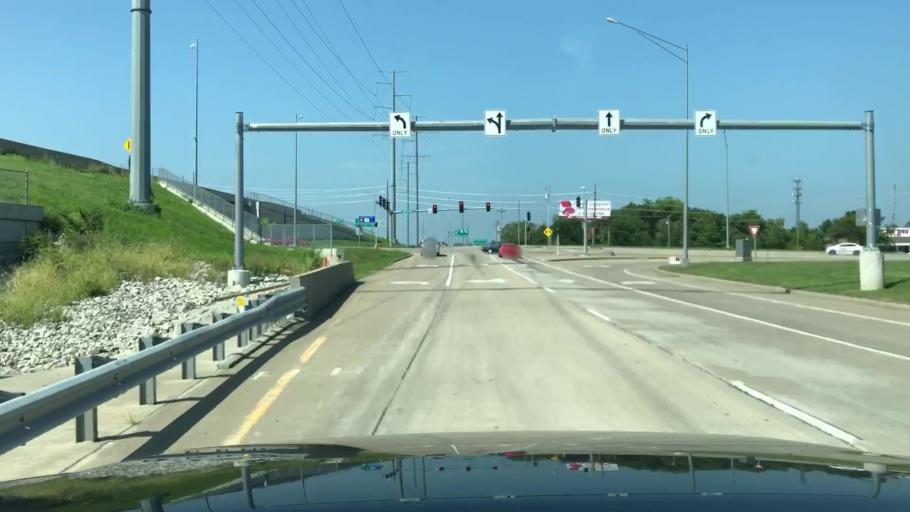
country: US
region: Missouri
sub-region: Saint Charles County
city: Saint Peters
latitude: 38.7480
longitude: -90.5903
